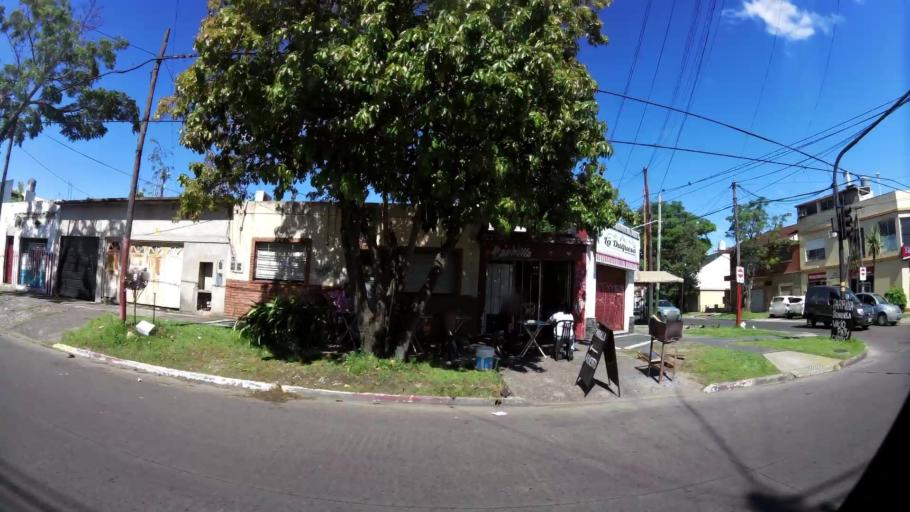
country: AR
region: Buenos Aires
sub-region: Partido de Lomas de Zamora
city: Lomas de Zamora
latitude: -34.7565
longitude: -58.4212
